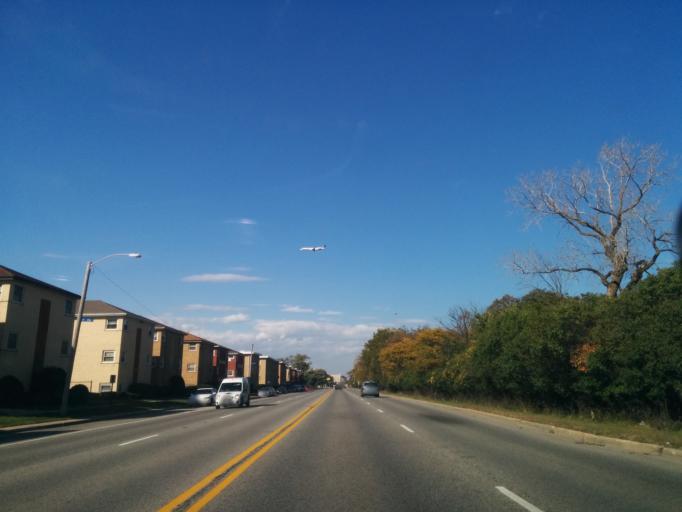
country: US
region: Illinois
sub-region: Cook County
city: Schiller Park
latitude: 41.9599
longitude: -87.8610
